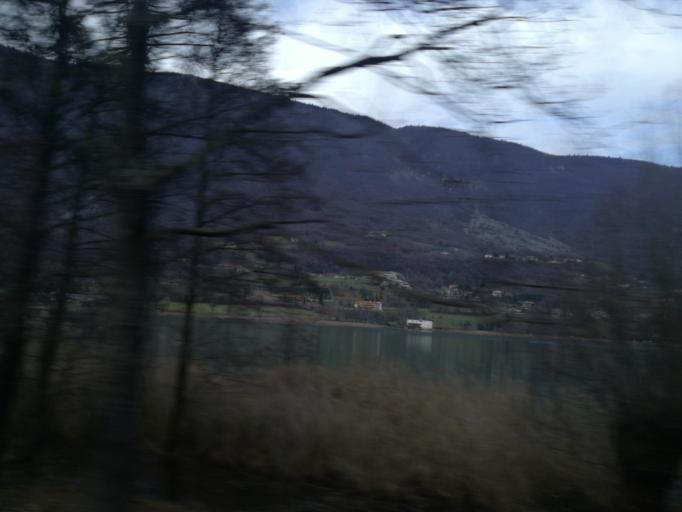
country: IT
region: Lombardy
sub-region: Provincia di Bergamo
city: Ranzanico
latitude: 45.7861
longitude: 9.9551
